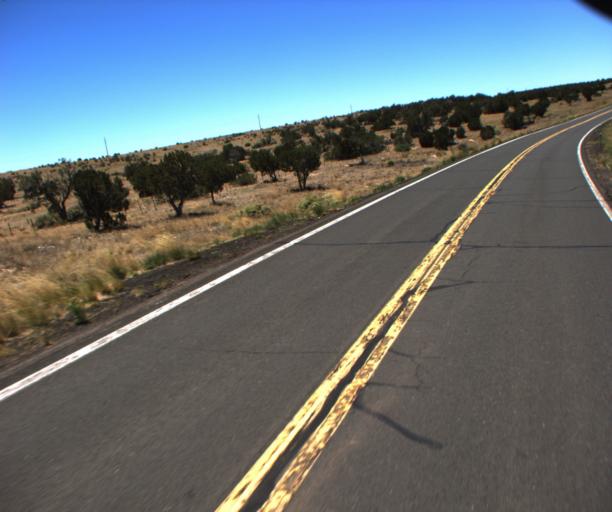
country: US
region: Arizona
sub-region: Coconino County
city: LeChee
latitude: 34.7687
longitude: -111.0087
